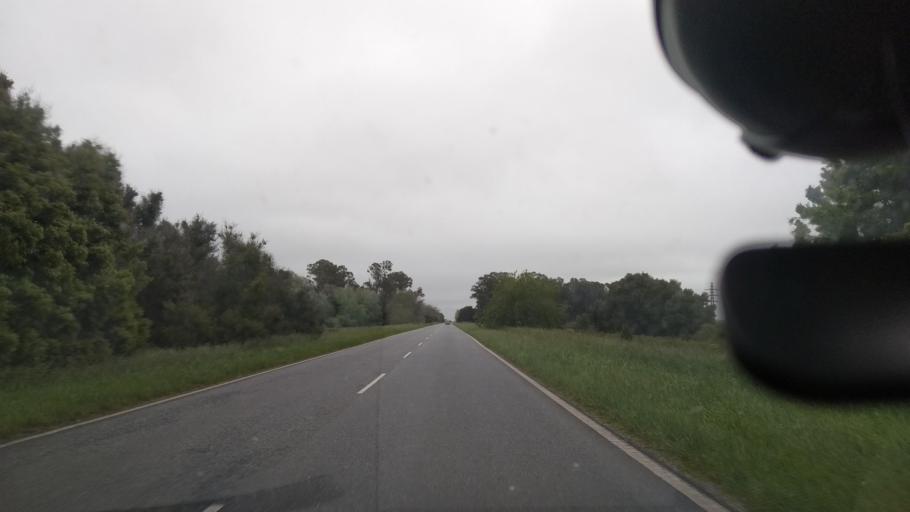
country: AR
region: Buenos Aires
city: Veronica
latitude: -35.3115
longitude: -57.4895
